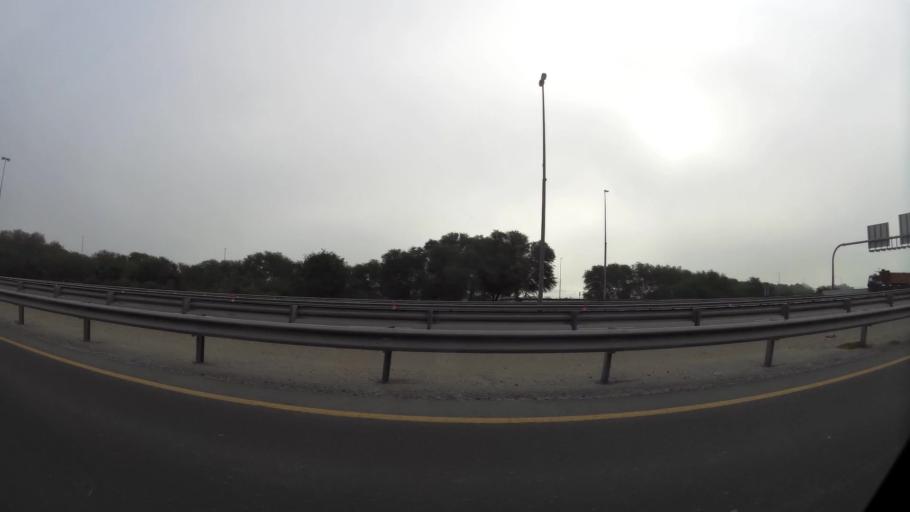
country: AE
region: Dubai
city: Dubai
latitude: 25.1816
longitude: 55.3140
